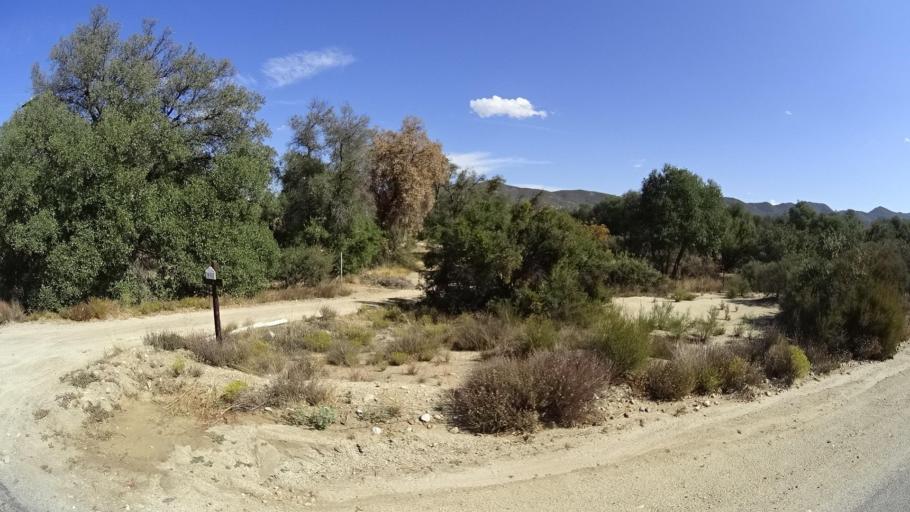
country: US
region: California
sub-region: Riverside County
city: Anza
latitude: 33.3849
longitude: -116.6754
